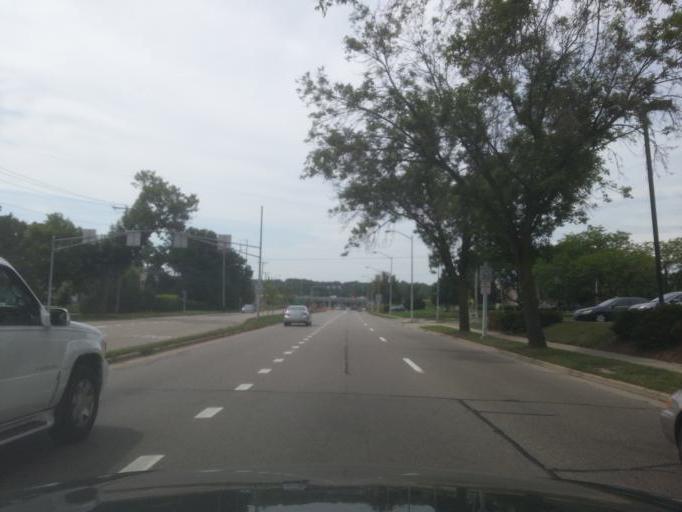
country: US
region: Wisconsin
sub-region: Dane County
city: Shorewood Hills
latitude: 43.0496
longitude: -89.4736
